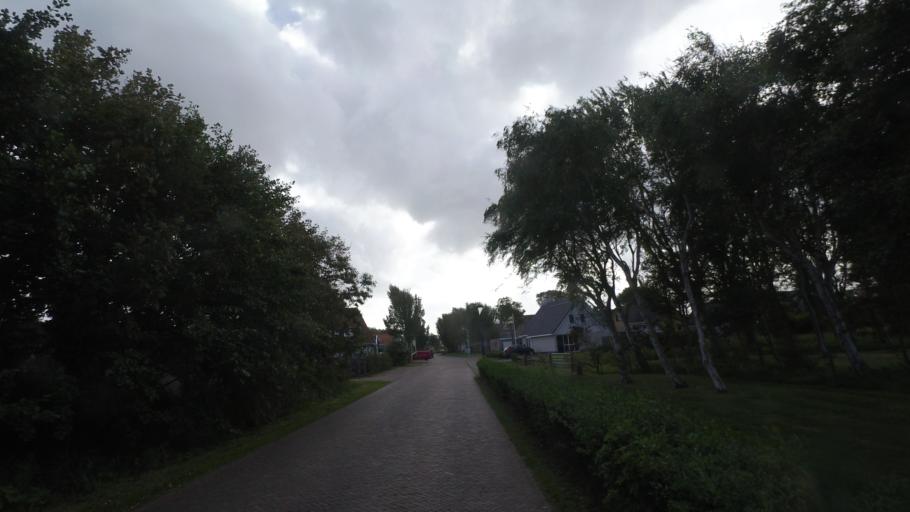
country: NL
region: Friesland
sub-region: Gemeente Ameland
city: Hollum
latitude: 53.4446
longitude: 5.6404
